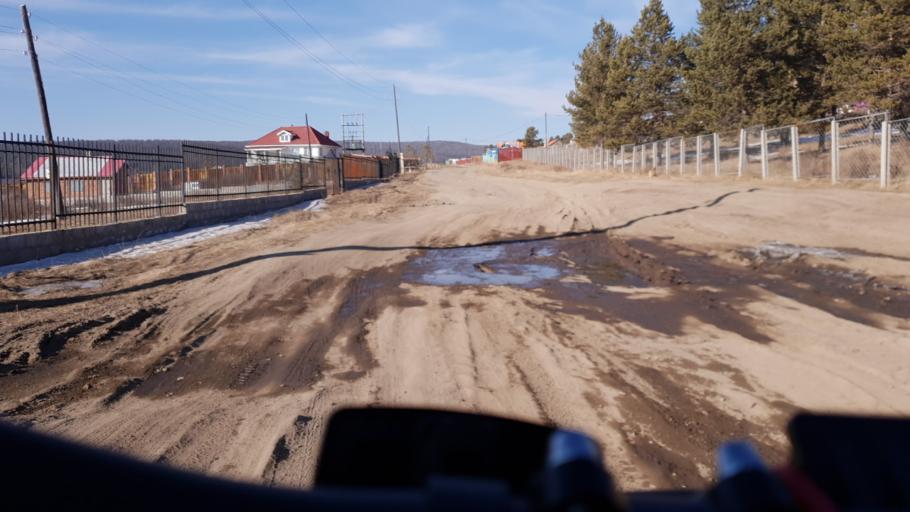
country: MN
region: Ulaanbaatar
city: Ulaanbaatar
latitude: 48.1503
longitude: 106.8864
